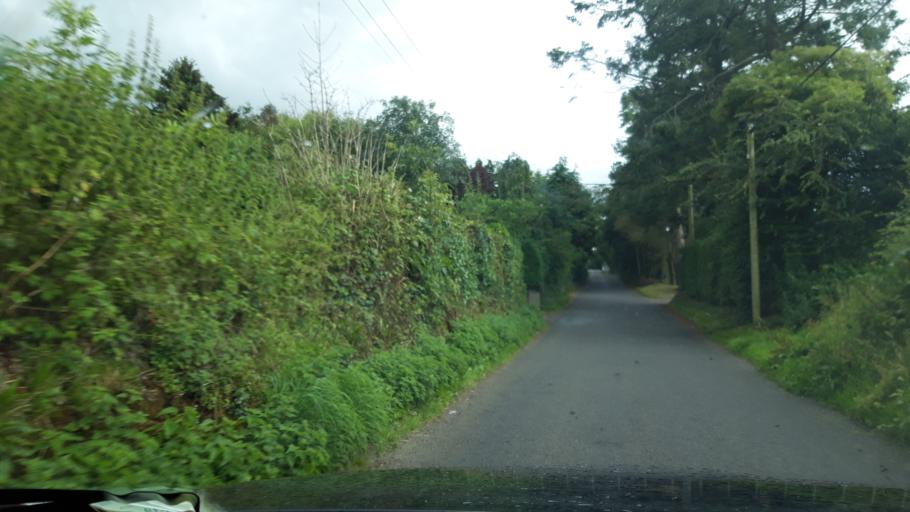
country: IE
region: Leinster
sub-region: Wicklow
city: Baltinglass
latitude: 52.9478
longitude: -6.7068
